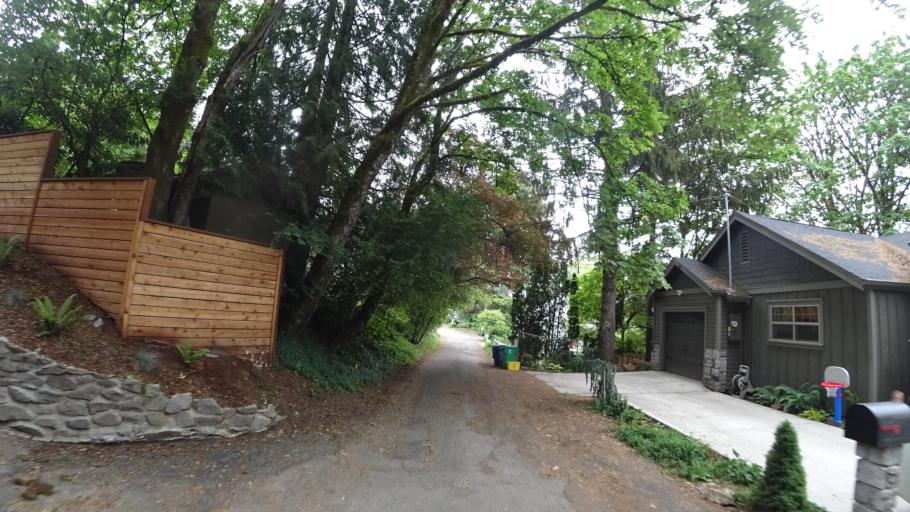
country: US
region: Oregon
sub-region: Multnomah County
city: Portland
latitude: 45.4977
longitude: -122.6931
